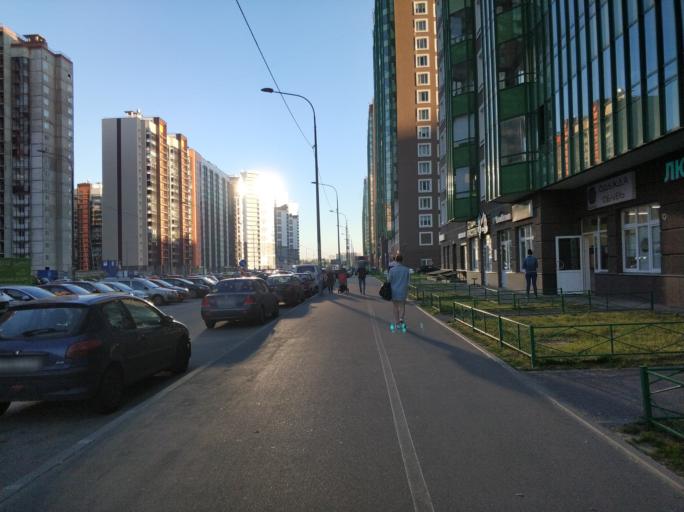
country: RU
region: Leningrad
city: Murino
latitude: 60.0567
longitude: 30.4278
